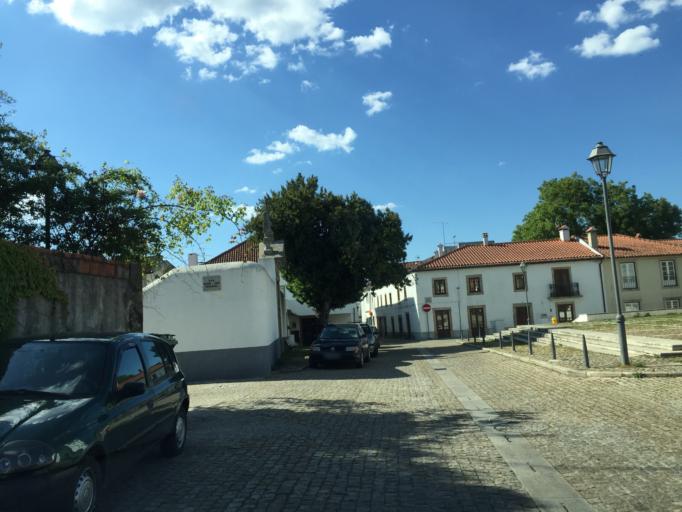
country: PT
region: Leiria
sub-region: Pedrogao Grande
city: Pedrogao Grande
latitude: 39.9165
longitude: -8.1455
